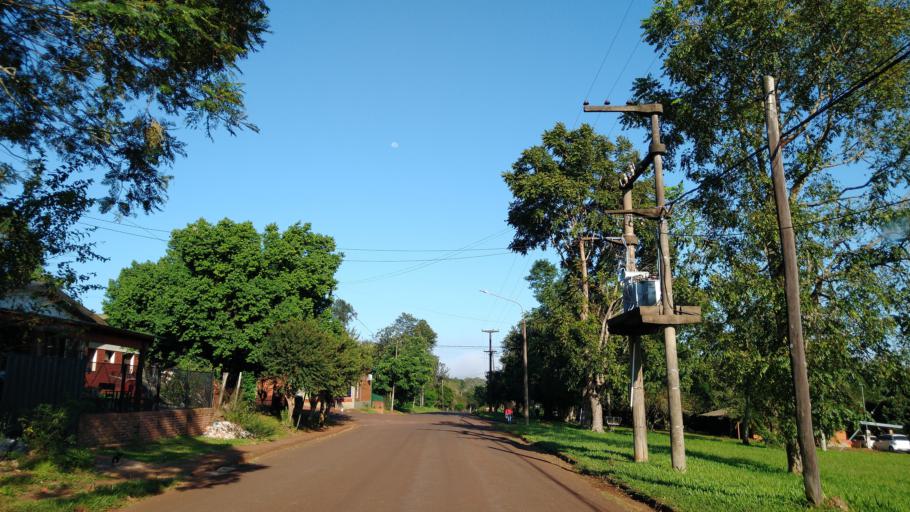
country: AR
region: Misiones
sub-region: Departamento de Montecarlo
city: Montecarlo
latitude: -26.5650
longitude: -54.7651
